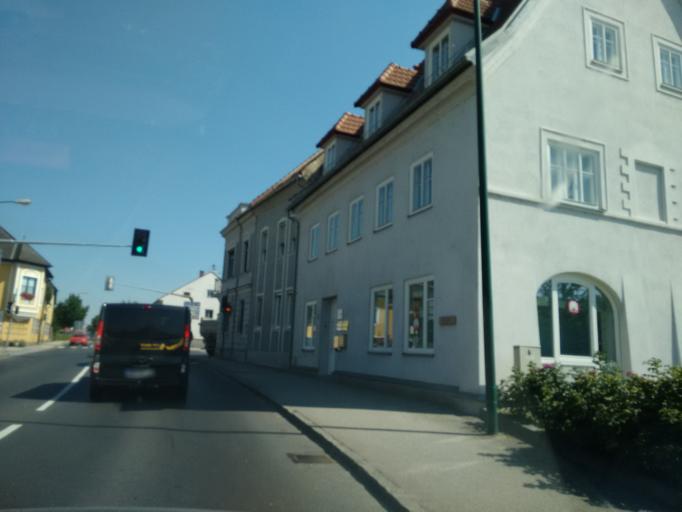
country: AT
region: Upper Austria
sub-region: Politischer Bezirk Urfahr-Umgebung
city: Feldkirchen an der Donau
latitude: 48.3083
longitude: 14.0202
